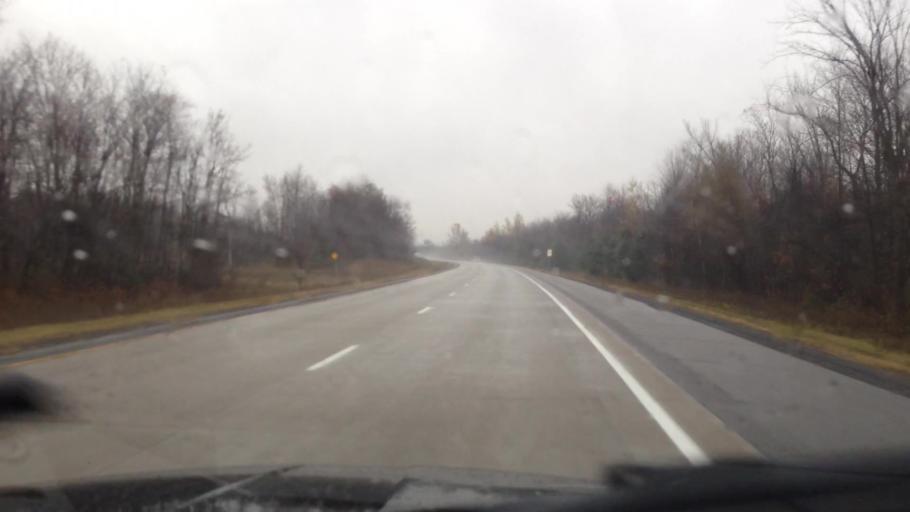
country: CA
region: Ontario
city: Casselman
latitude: 45.3813
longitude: -74.8054
